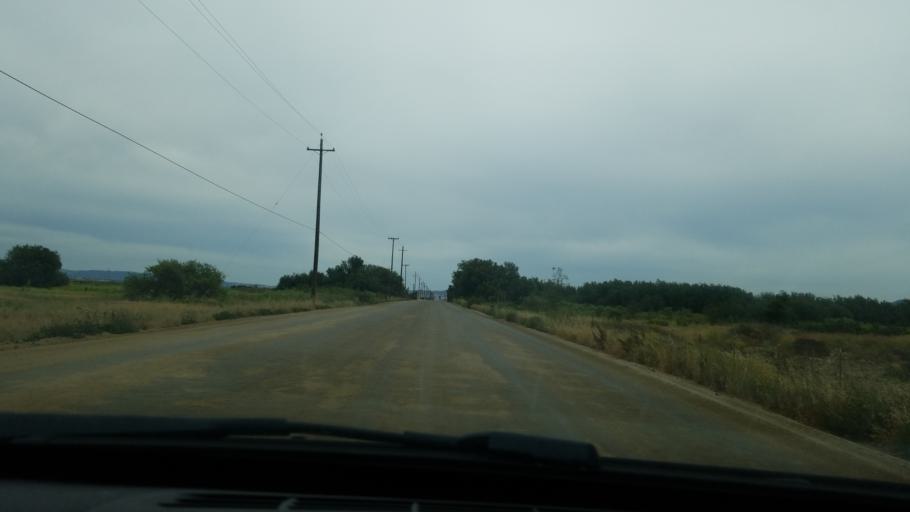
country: US
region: California
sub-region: Santa Barbara County
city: Guadalupe
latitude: 34.9831
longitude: -120.5131
